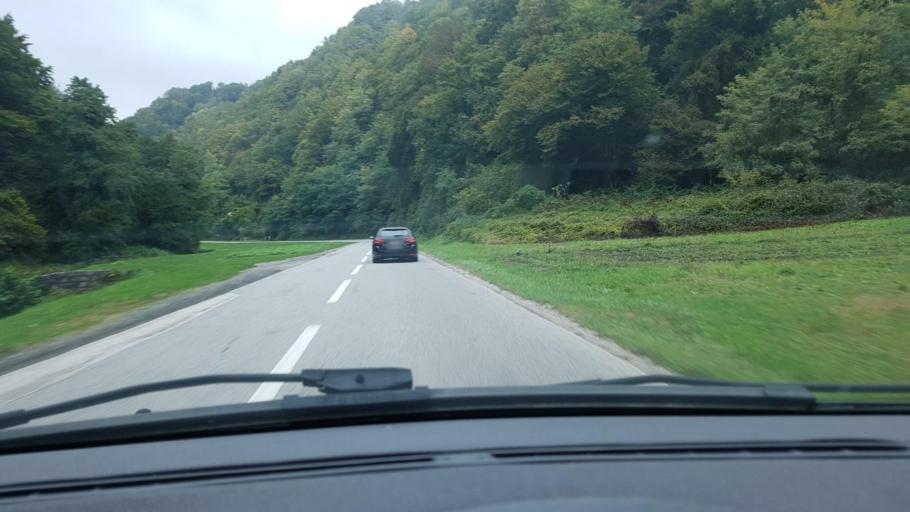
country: HR
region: Krapinsko-Zagorska
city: Marija Bistrica
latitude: 45.9373
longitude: 16.1123
